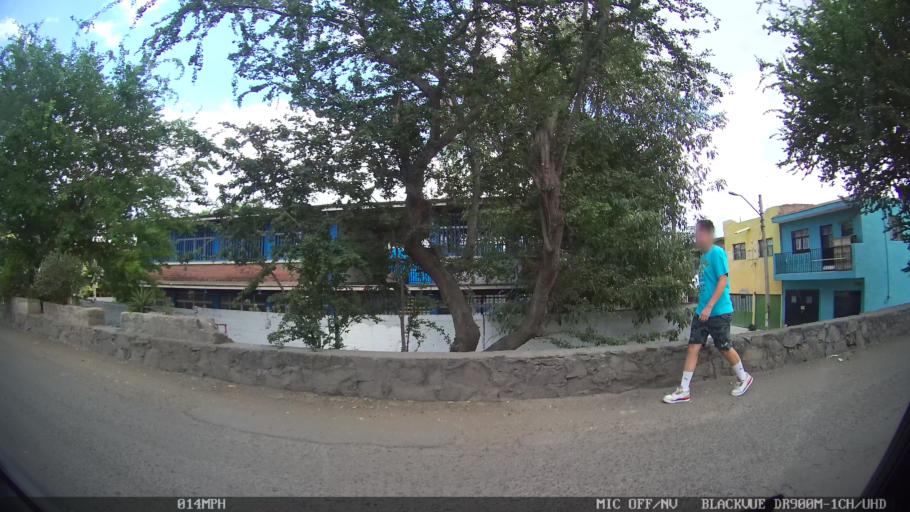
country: MX
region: Jalisco
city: Tonala
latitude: 20.6530
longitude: -103.2562
